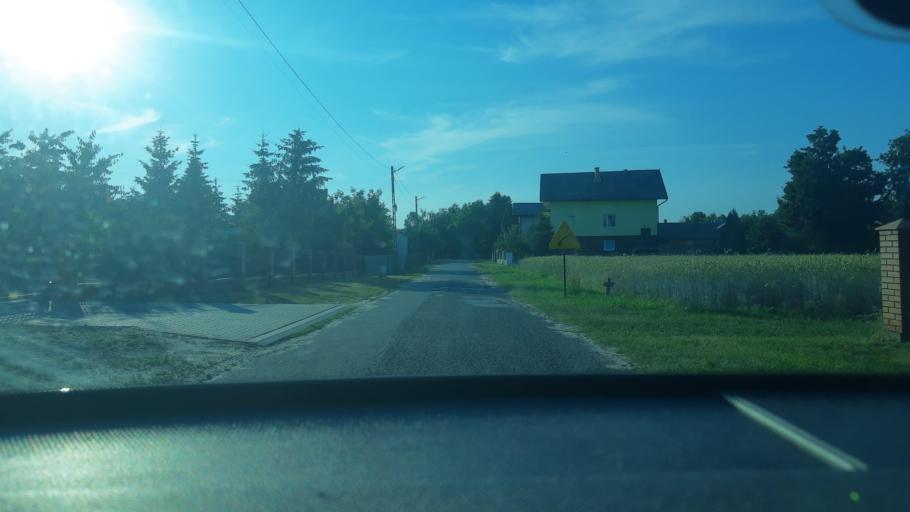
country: PL
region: Lodz Voivodeship
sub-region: Powiat sieradzki
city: Sieradz
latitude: 51.5433
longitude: 18.7555
